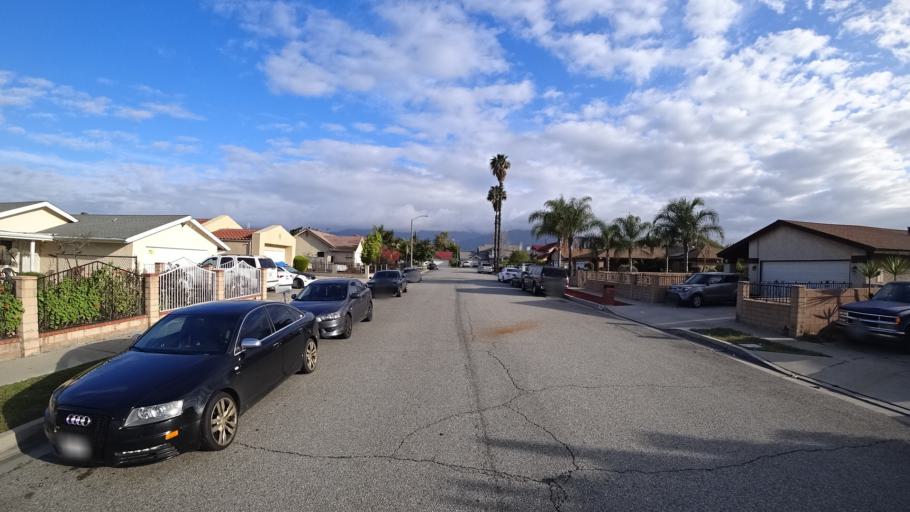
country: US
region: California
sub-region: Los Angeles County
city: Baldwin Park
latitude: 34.0979
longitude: -117.9726
